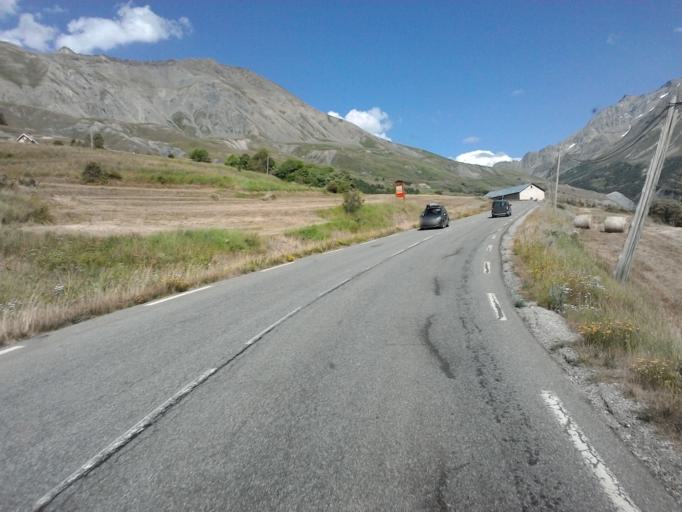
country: FR
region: Rhone-Alpes
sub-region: Departement de la Savoie
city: Valloire
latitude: 45.0413
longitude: 6.3433
